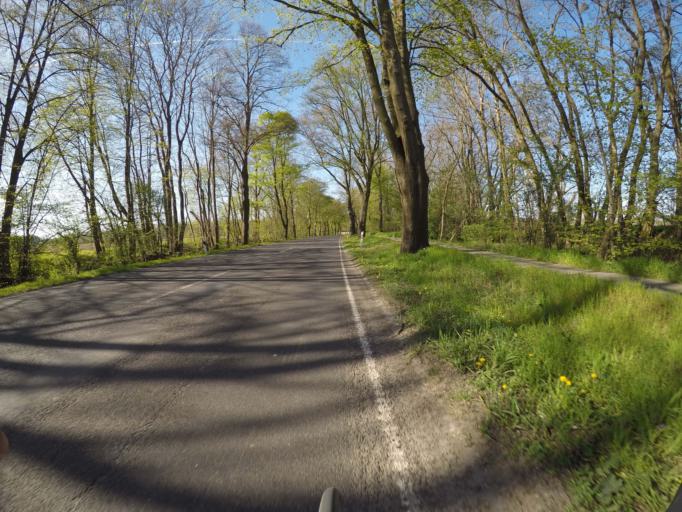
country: DE
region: Brandenburg
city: Grunheide
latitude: 52.4664
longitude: 13.8576
